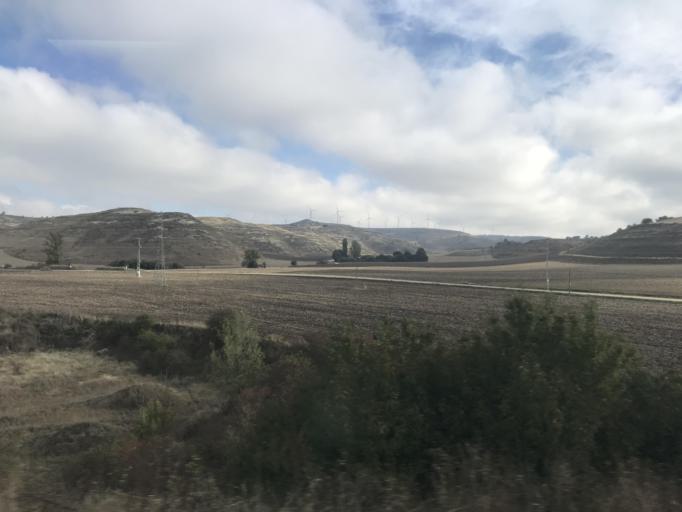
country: ES
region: Castille and Leon
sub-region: Provincia de Burgos
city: Santa Maria del Invierno
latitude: 42.4358
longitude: -3.4377
